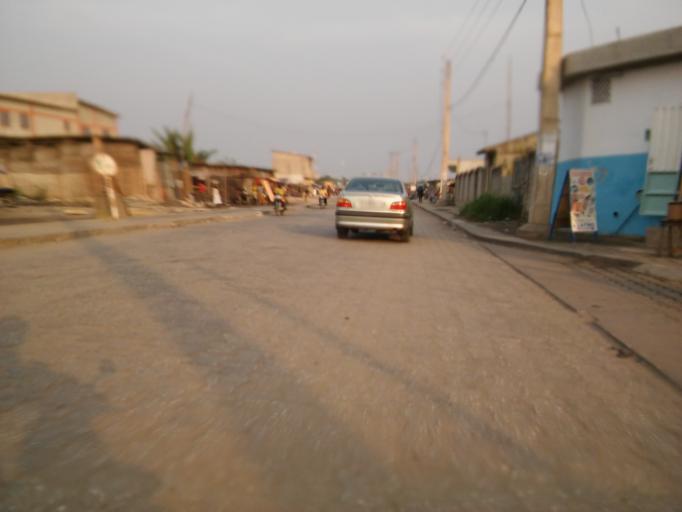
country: BJ
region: Atlantique
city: Abomey-Calavi
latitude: 6.3933
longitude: 2.3535
